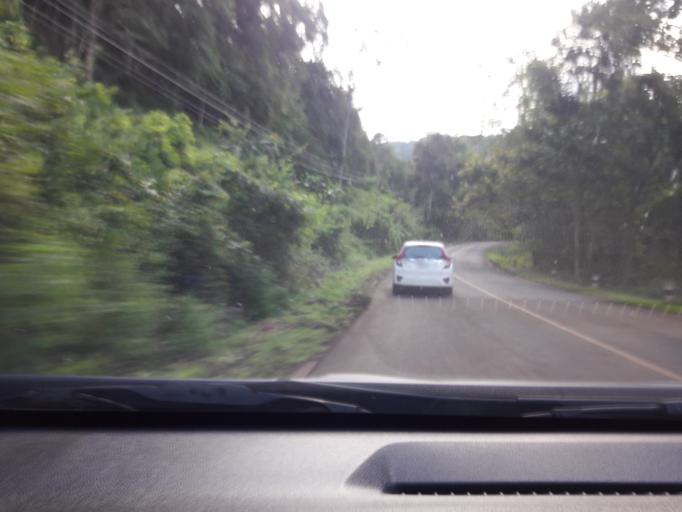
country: TH
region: Mae Hong Son
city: Sop Pong
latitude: 19.5609
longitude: 98.1933
